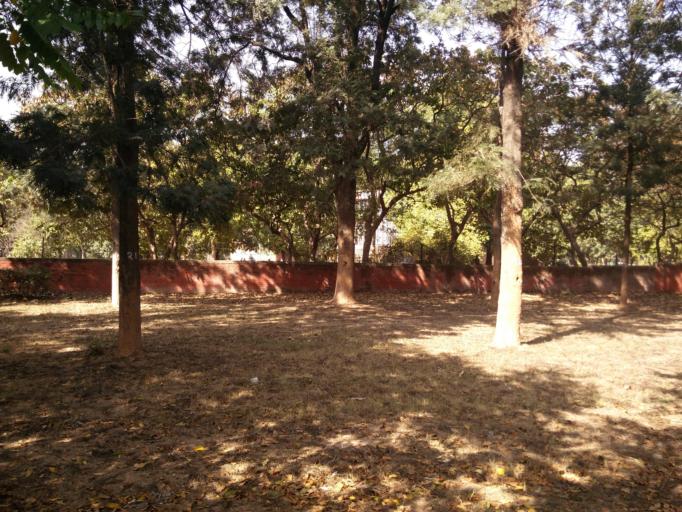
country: IN
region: Chandigarh
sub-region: Chandigarh
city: Chandigarh
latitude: 30.7474
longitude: 76.7863
